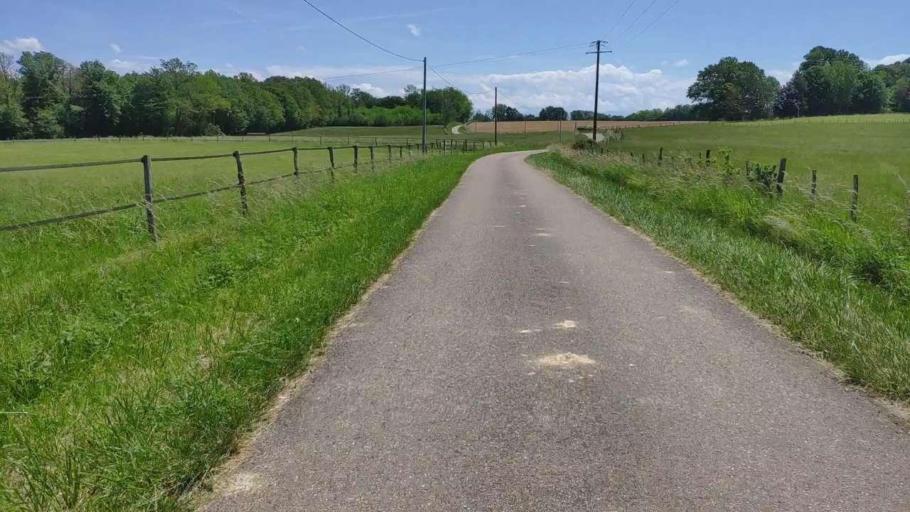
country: FR
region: Franche-Comte
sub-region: Departement du Jura
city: Bletterans
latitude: 46.7904
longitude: 5.3968
